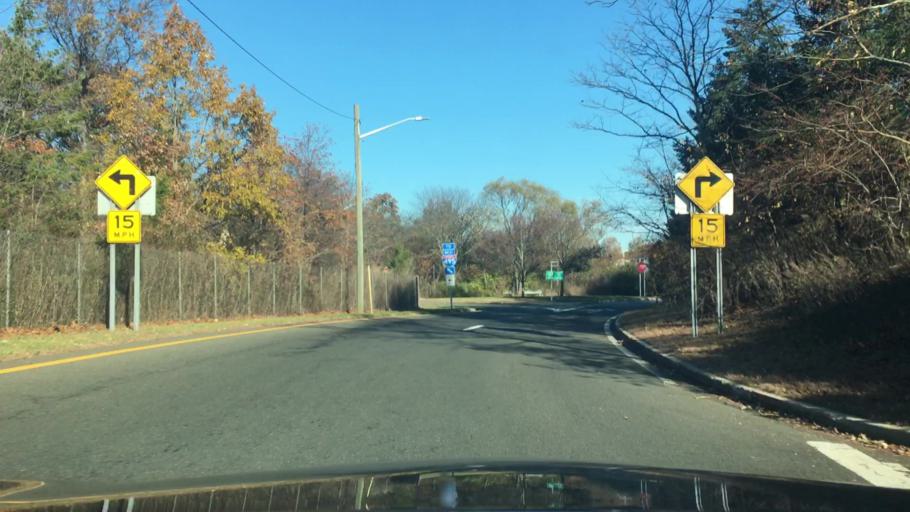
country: US
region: New York
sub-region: Nassau County
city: Syosset
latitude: 40.8025
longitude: -73.4892
